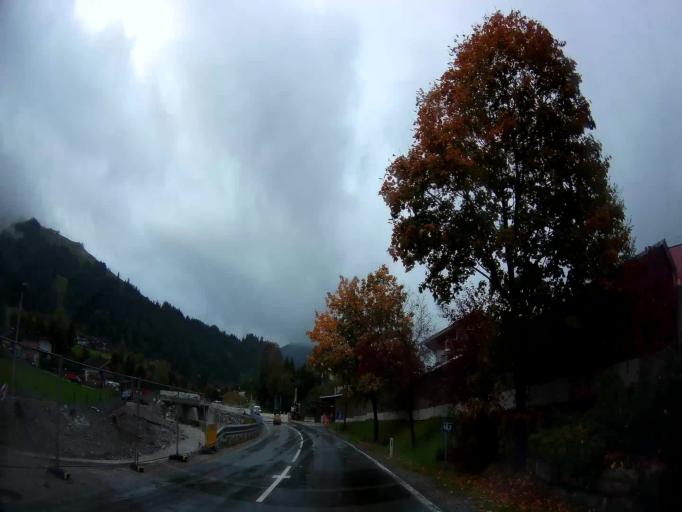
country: AT
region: Salzburg
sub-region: Politischer Bezirk Zell am See
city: Leogang
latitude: 47.4408
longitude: 12.7291
